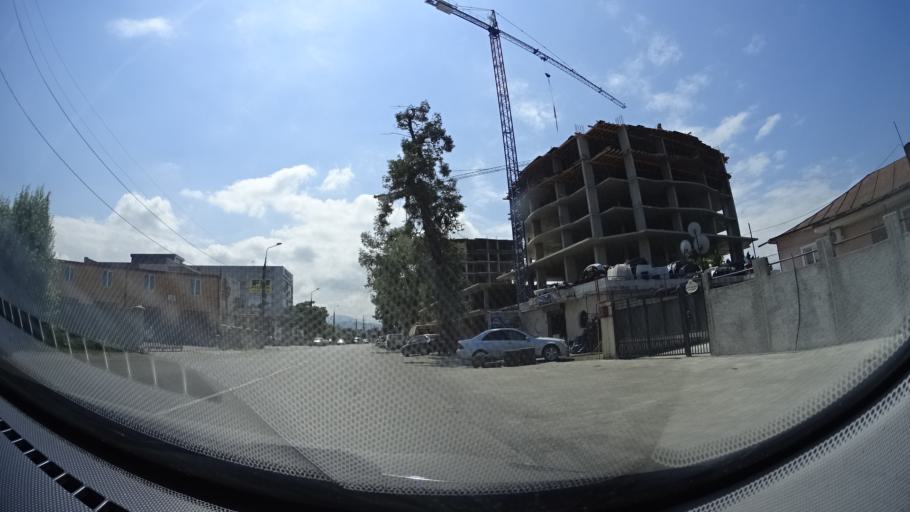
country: GE
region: Ajaria
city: Batumi
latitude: 41.6231
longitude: 41.6141
